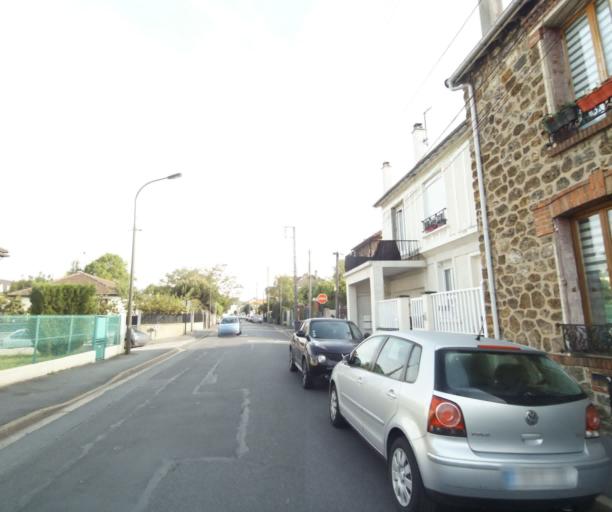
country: FR
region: Ile-de-France
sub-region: Departement du Val-d'Oise
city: Argenteuil
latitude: 48.9533
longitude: 2.2571
